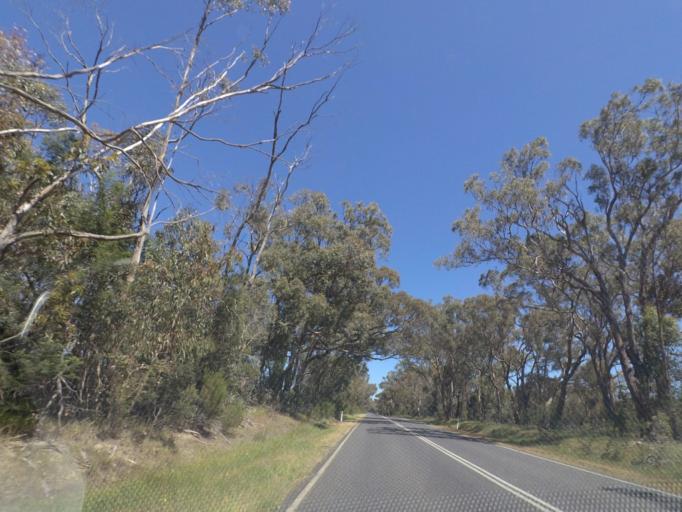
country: AU
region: Victoria
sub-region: Hume
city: Sunbury
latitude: -37.3026
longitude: 144.8649
